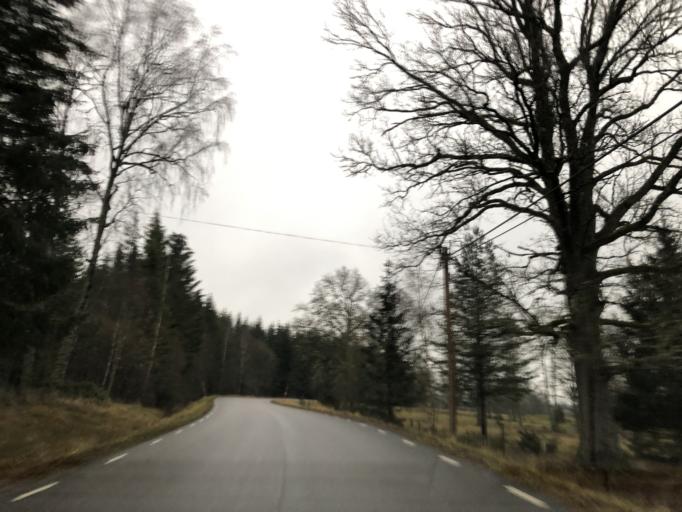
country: SE
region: Vaestra Goetaland
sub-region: Ulricehamns Kommun
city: Ulricehamn
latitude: 57.8490
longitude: 13.2607
